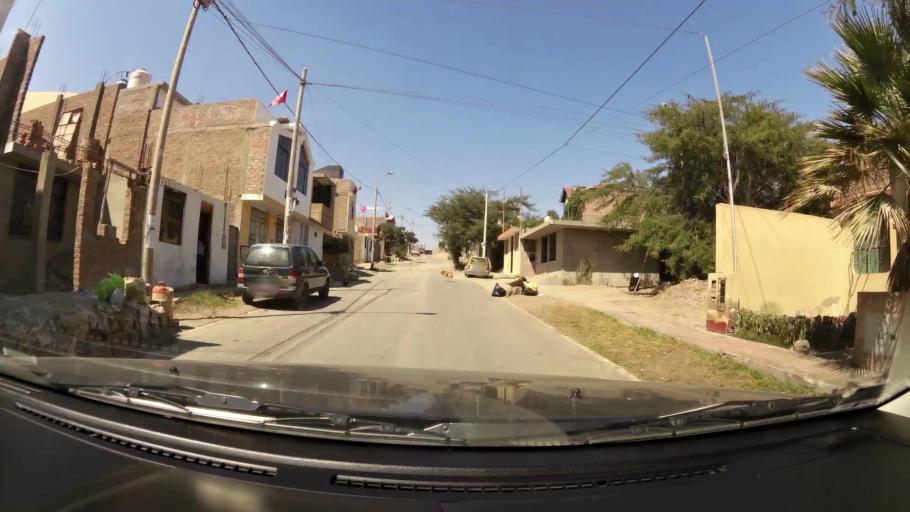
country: PE
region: Ica
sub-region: Provincia de Ica
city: Subtanjalla
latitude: -14.0400
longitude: -75.7481
